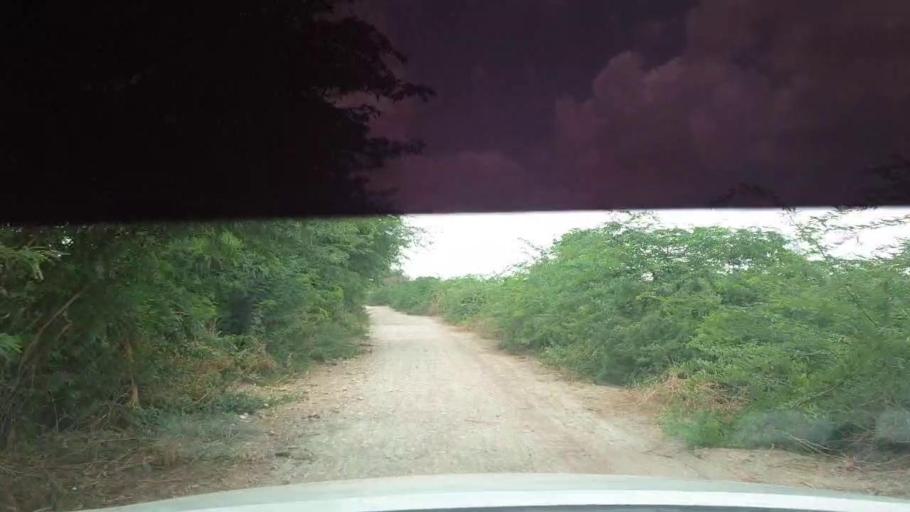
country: PK
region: Sindh
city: Kadhan
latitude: 24.4642
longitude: 69.0465
